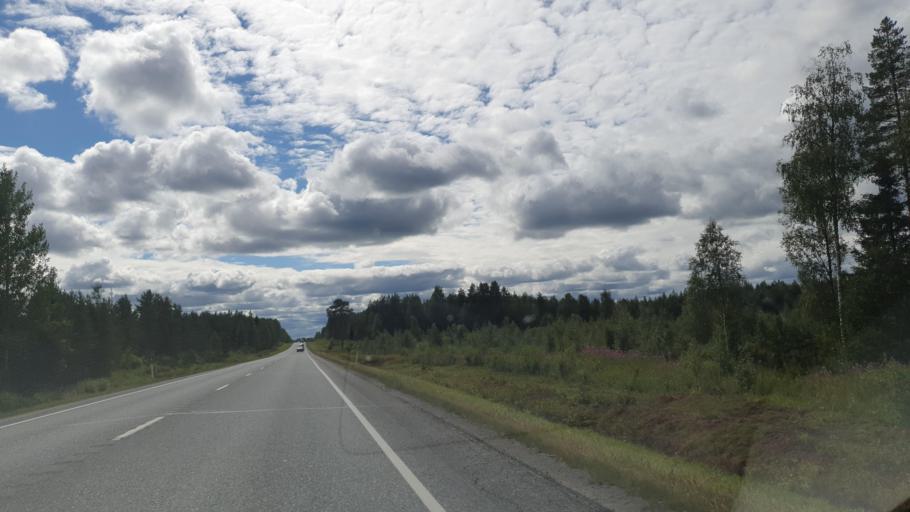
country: FI
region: Kainuu
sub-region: Kajaani
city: Kajaani
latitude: 64.1334
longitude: 27.4851
